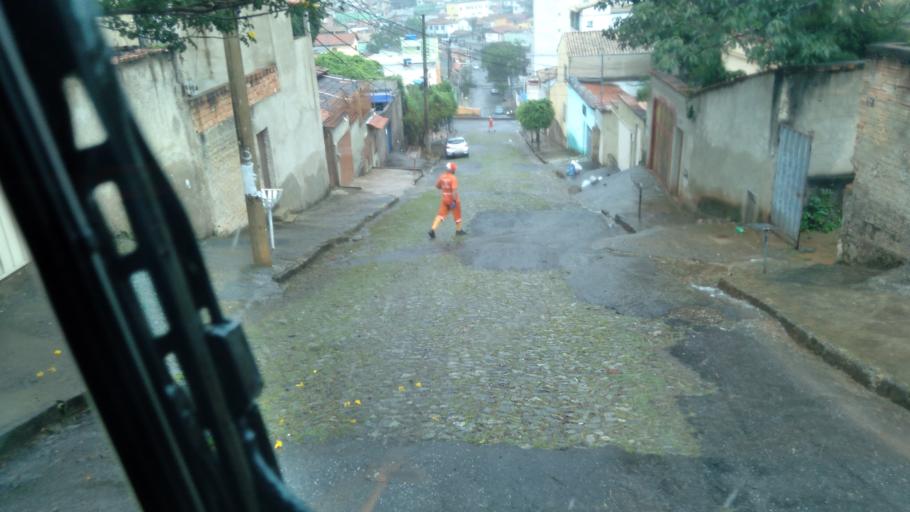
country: BR
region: Minas Gerais
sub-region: Belo Horizonte
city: Belo Horizonte
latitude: -19.9257
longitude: -43.9059
